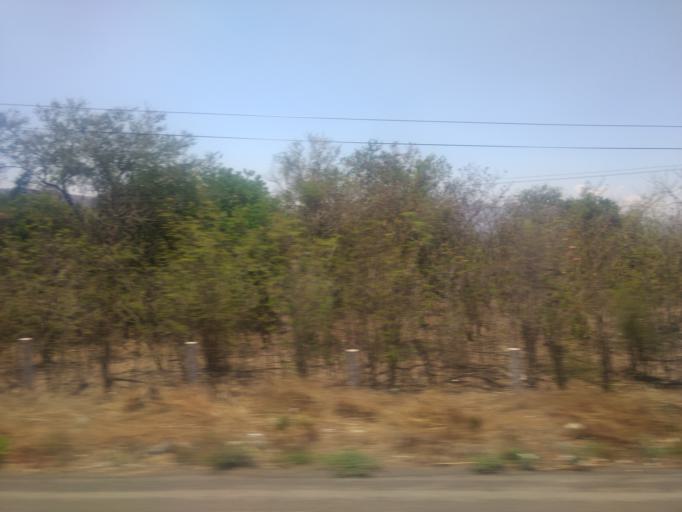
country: MX
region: Colima
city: Coquimatlan
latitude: 19.1369
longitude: -103.7721
